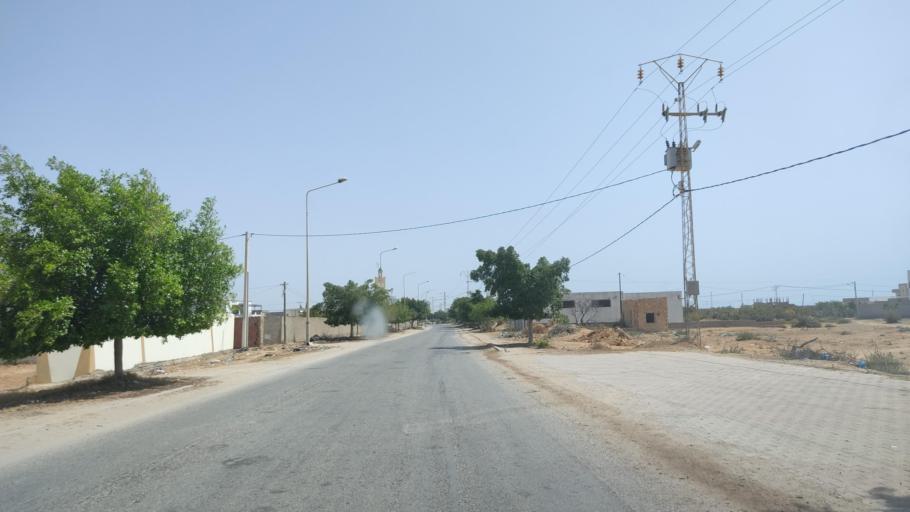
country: TN
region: Safaqis
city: Sfax
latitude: 34.6704
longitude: 10.7135
